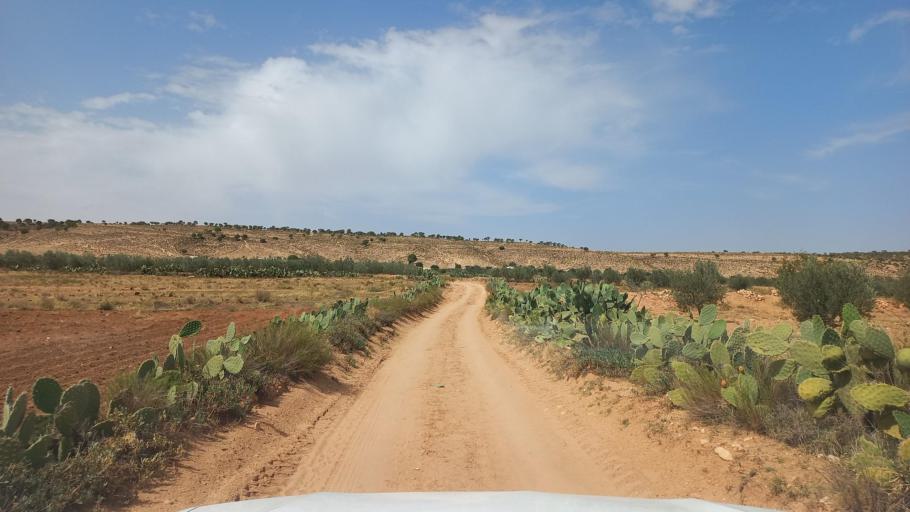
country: TN
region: Al Qasrayn
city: Kasserine
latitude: 35.3672
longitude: 8.8805
